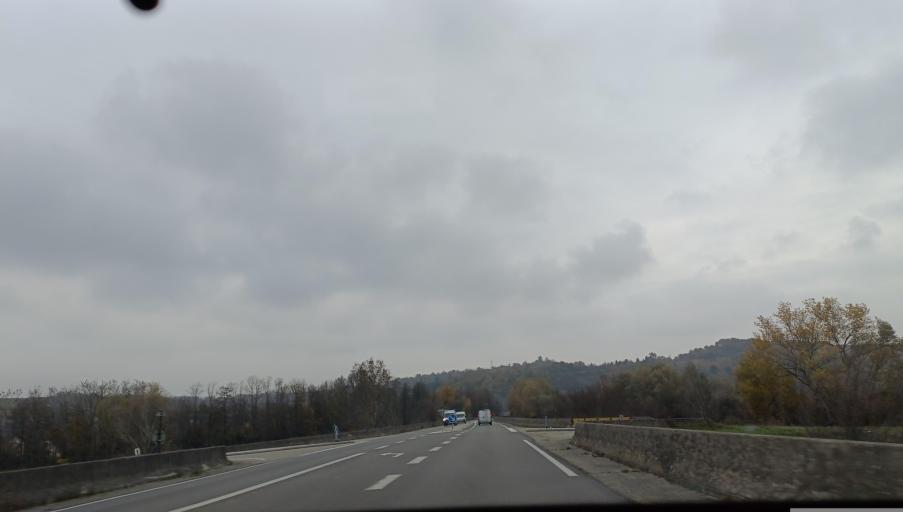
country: FR
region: Rhone-Alpes
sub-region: Departement de l'Isere
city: Pont-Eveque
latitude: 45.5387
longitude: 4.9264
